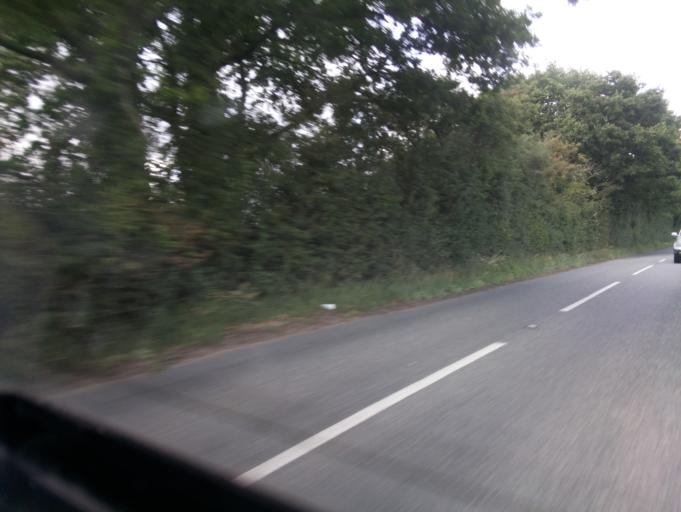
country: GB
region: England
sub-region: Gloucestershire
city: Moreton in Marsh
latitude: 52.0525
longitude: -1.6970
